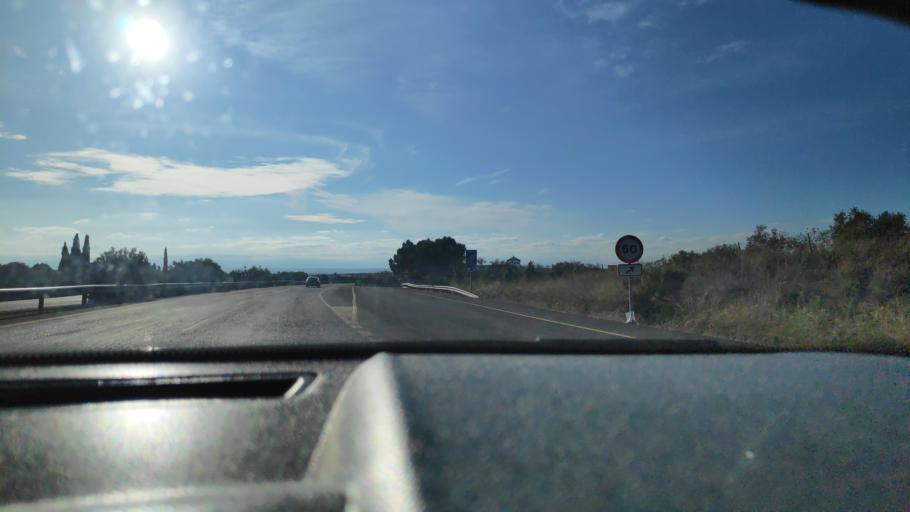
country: ES
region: Andalusia
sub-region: Provincia de Sevilla
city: Ecija
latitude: 37.5765
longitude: -4.9994
